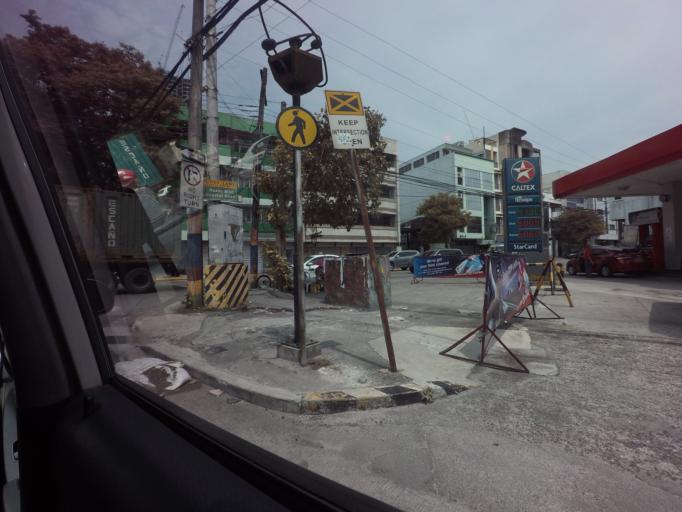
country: PH
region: Metro Manila
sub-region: City of Manila
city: Port Area
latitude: 14.5726
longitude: 120.9932
